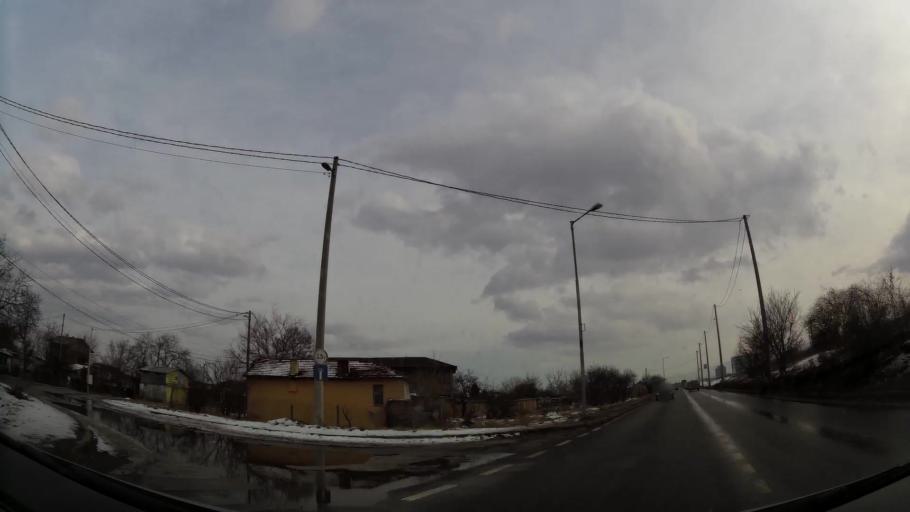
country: BG
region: Sofia-Capital
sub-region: Stolichna Obshtina
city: Sofia
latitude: 42.6915
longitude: 23.3861
